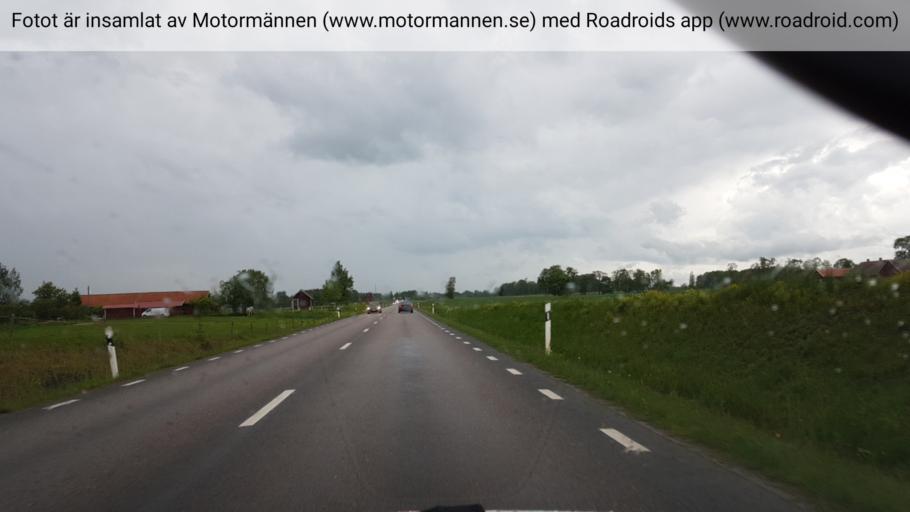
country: SE
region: Vaestra Goetaland
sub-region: Tibro Kommun
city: Tibro
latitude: 58.3523
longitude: 14.0718
